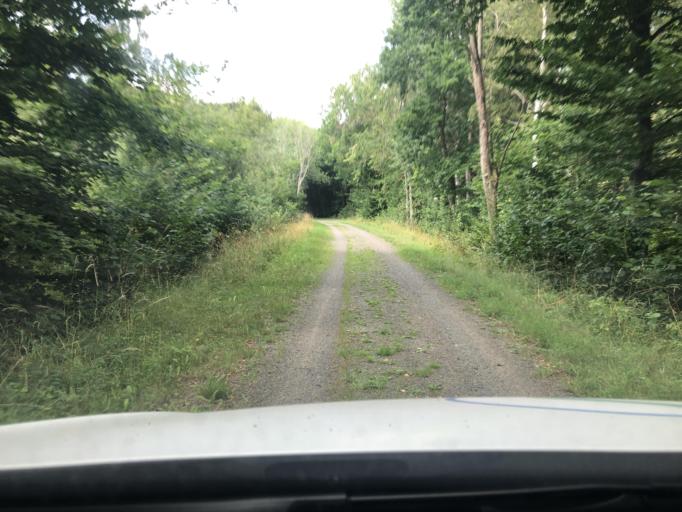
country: SE
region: Skane
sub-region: Kristianstads Kommun
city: Degeberga
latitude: 55.7823
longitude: 14.1730
